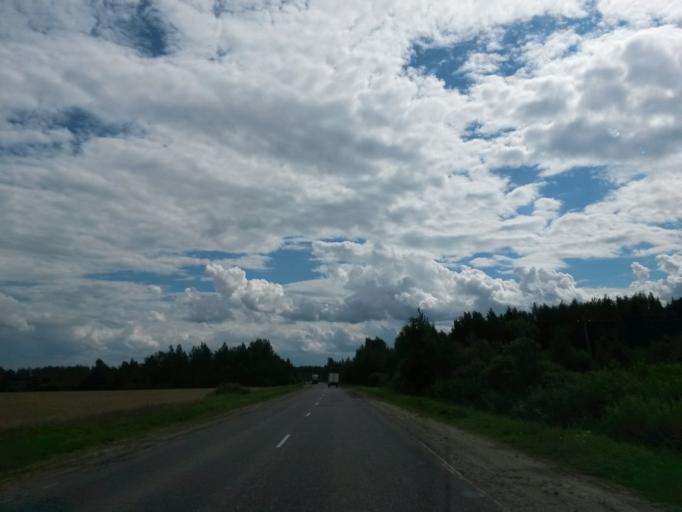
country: RU
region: Ivanovo
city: Novo-Talitsy
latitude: 57.0388
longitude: 40.7443
